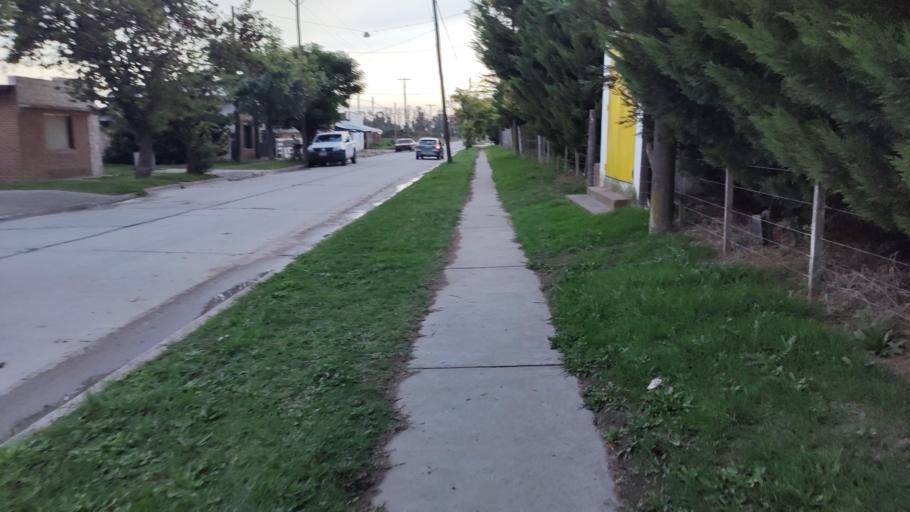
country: AR
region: Buenos Aires
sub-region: Partido de Loberia
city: Loberia
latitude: -38.1760
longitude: -58.7763
